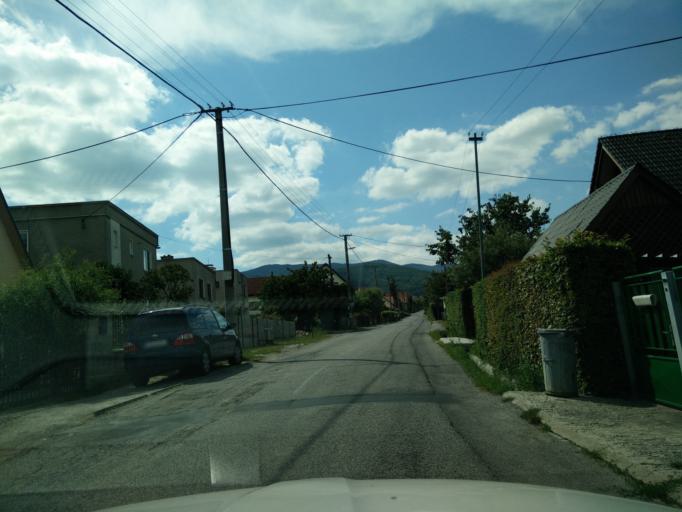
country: SK
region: Nitriansky
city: Bojnice
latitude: 48.8268
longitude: 18.6027
